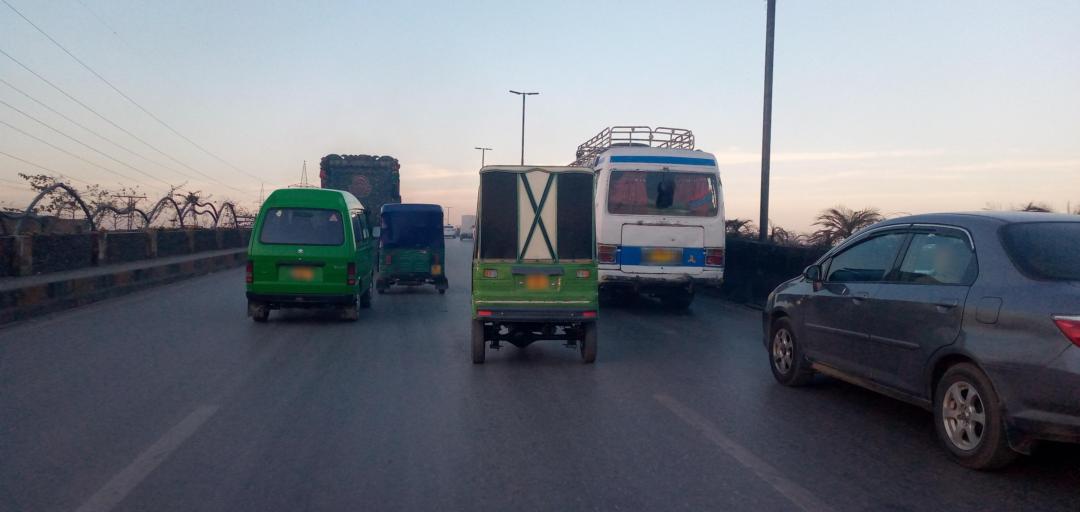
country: PK
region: Khyber Pakhtunkhwa
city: Peshawar
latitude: 34.0184
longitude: 71.6219
